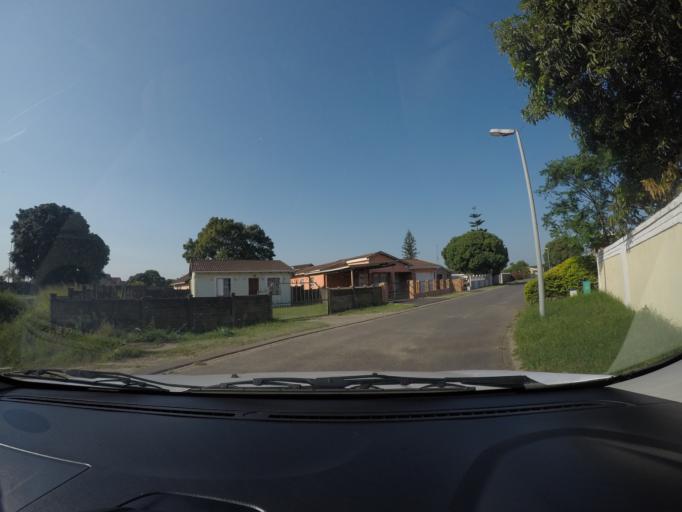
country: ZA
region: KwaZulu-Natal
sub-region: uThungulu District Municipality
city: Richards Bay
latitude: -28.7157
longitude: 32.0373
